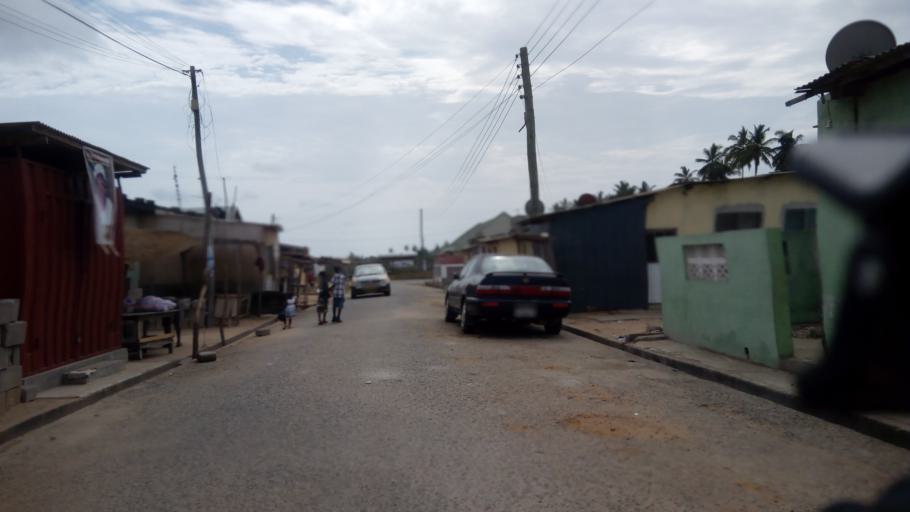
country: GH
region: Central
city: Cape Coast
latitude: 5.1016
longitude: -1.2762
